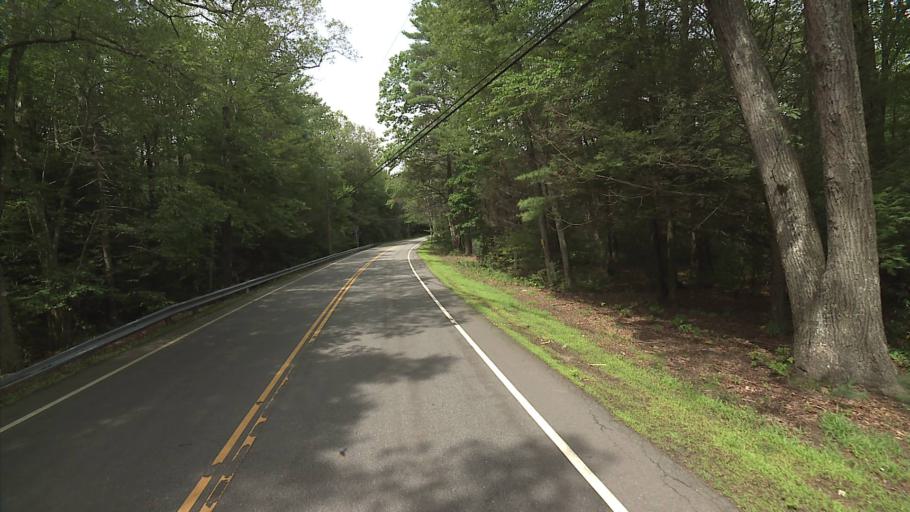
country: US
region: Massachusetts
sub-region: Hampden County
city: Holland
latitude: 41.9420
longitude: -72.1032
